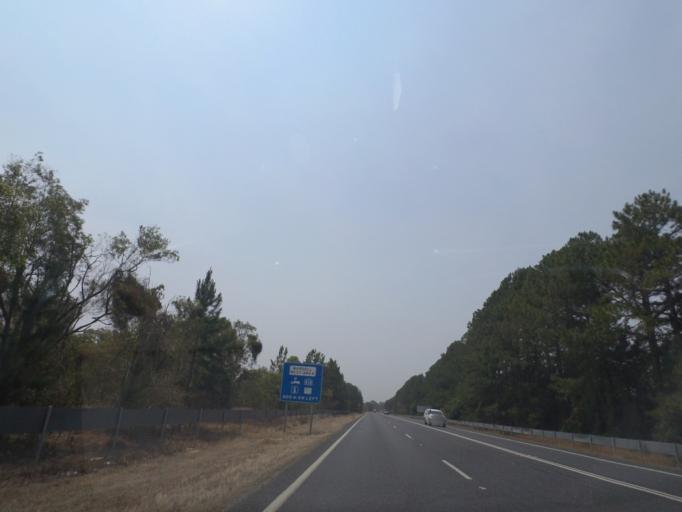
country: AU
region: New South Wales
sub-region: Ballina
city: Ballina
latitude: -28.9407
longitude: 153.4694
